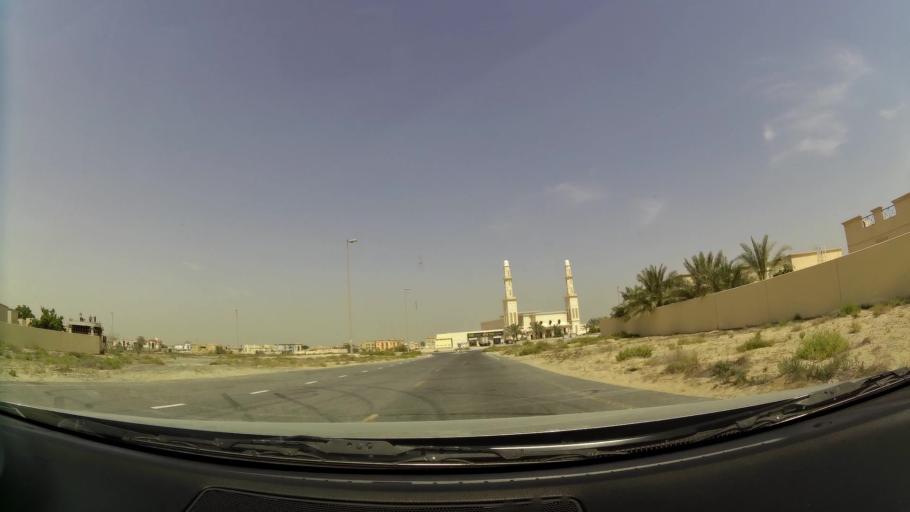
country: AE
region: Ash Shariqah
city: Sharjah
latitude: 25.1858
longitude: 55.4405
